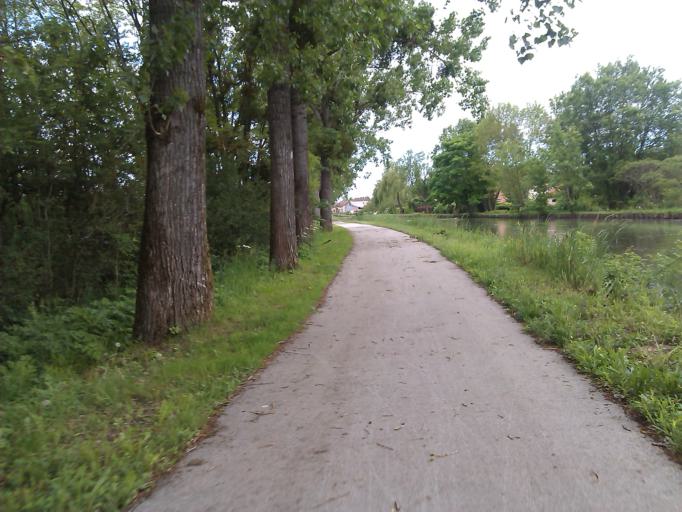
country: FR
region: Bourgogne
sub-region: Departement de Saone-et-Loire
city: Virey-le-Grand
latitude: 46.8288
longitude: 4.8501
